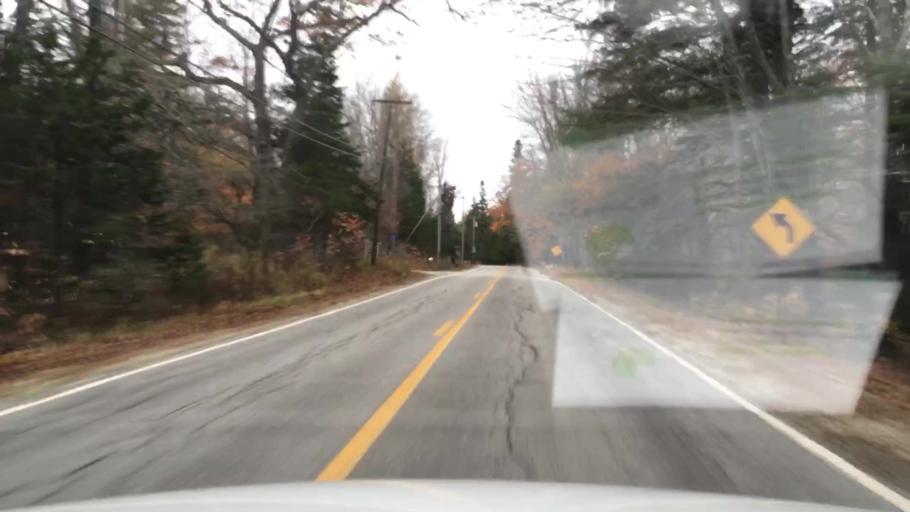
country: US
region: Maine
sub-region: Hancock County
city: Sedgwick
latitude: 44.3666
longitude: -68.5534
